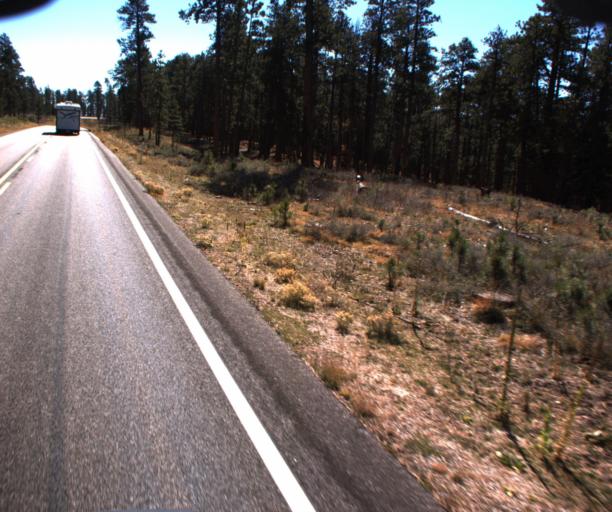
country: US
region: Arizona
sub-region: Coconino County
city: Fredonia
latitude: 36.6421
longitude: -112.1754
